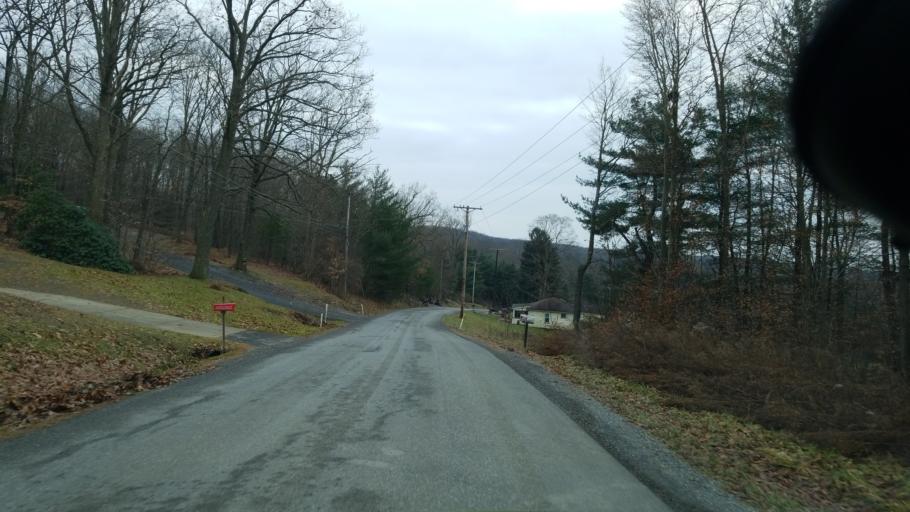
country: US
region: Pennsylvania
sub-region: Clearfield County
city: Treasure Lake
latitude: 41.1224
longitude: -78.6894
